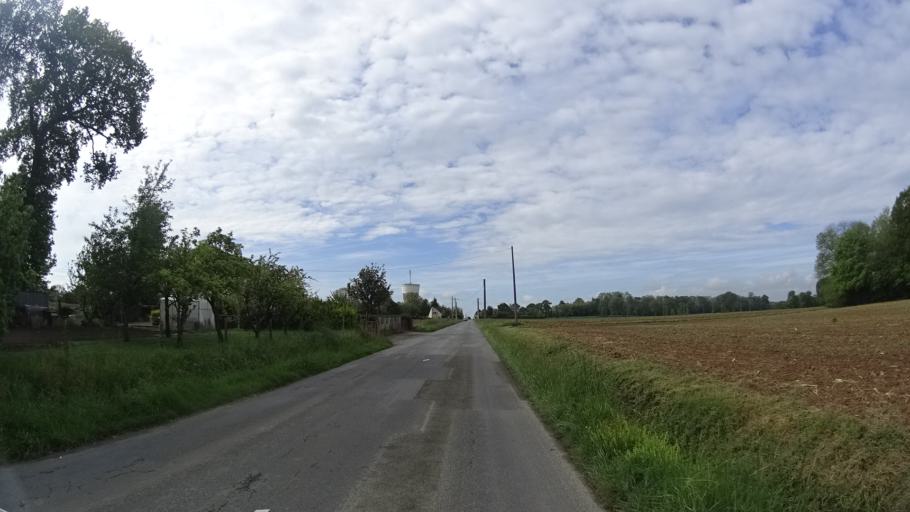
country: FR
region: Brittany
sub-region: Departement d'Ille-et-Vilaine
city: Mordelles
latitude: 48.0832
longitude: -1.8424
